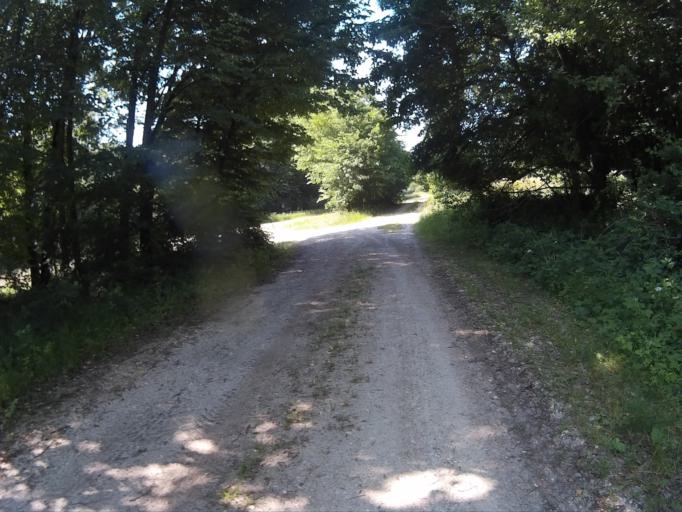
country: AT
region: Burgenland
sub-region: Politischer Bezirk Gussing
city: Heiligenbrunn
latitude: 46.9073
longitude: 16.4631
